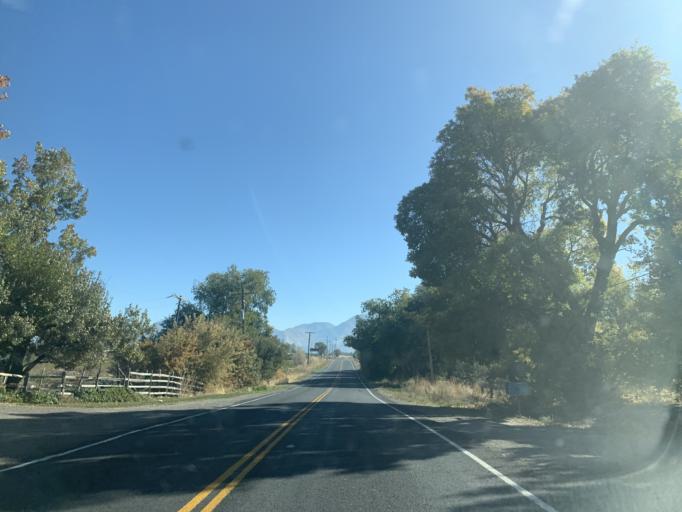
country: US
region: Utah
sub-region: Utah County
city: West Mountain
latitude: 40.0411
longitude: -111.7709
